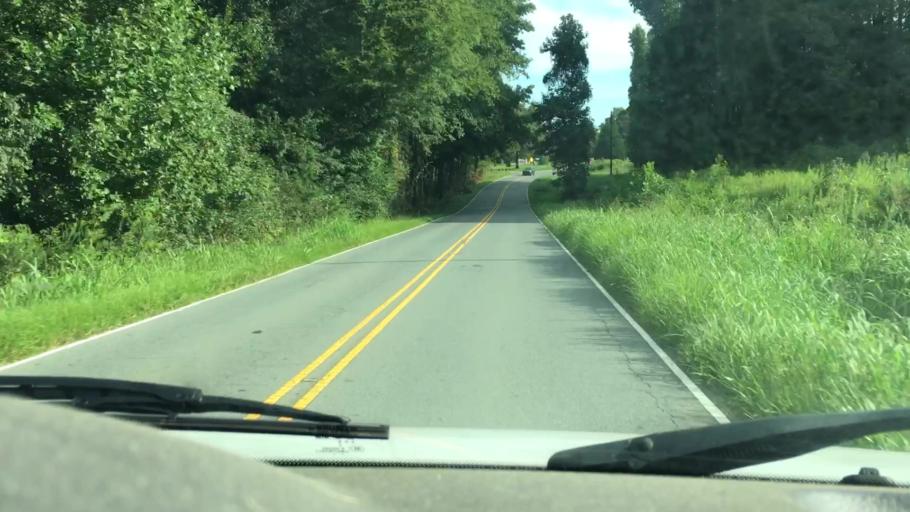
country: US
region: North Carolina
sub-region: Mecklenburg County
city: Huntersville
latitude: 35.3622
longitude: -80.8204
